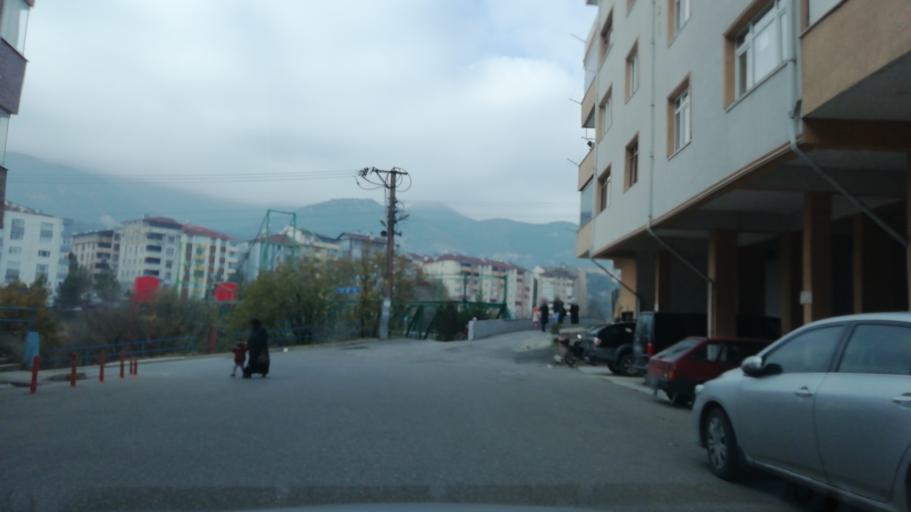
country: TR
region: Karabuk
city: Karabuk
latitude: 41.2069
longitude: 32.6259
